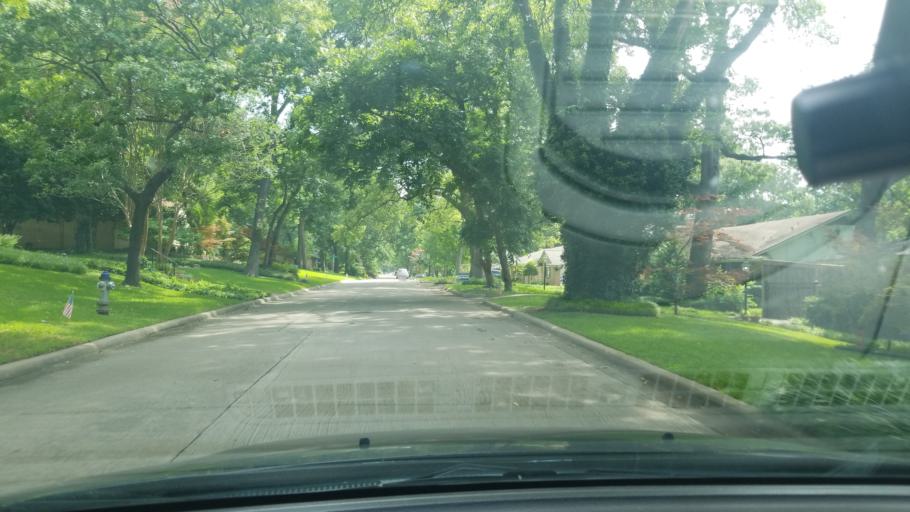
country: US
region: Texas
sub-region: Dallas County
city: Highland Park
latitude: 32.8086
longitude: -96.7160
